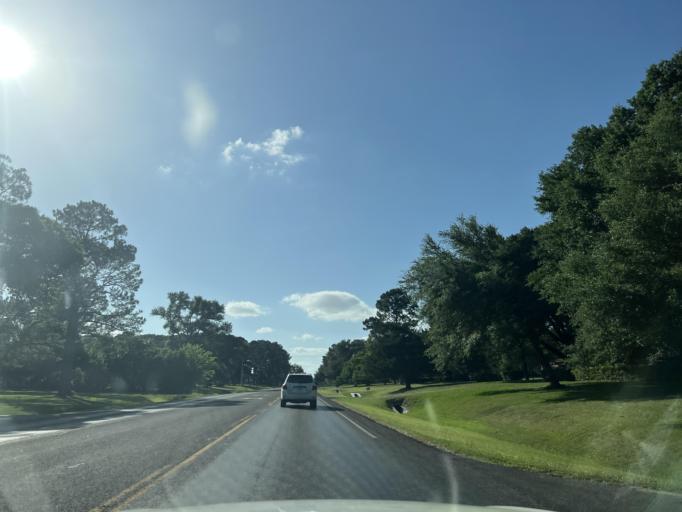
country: US
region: Texas
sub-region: Washington County
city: Brenham
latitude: 30.1491
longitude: -96.3642
